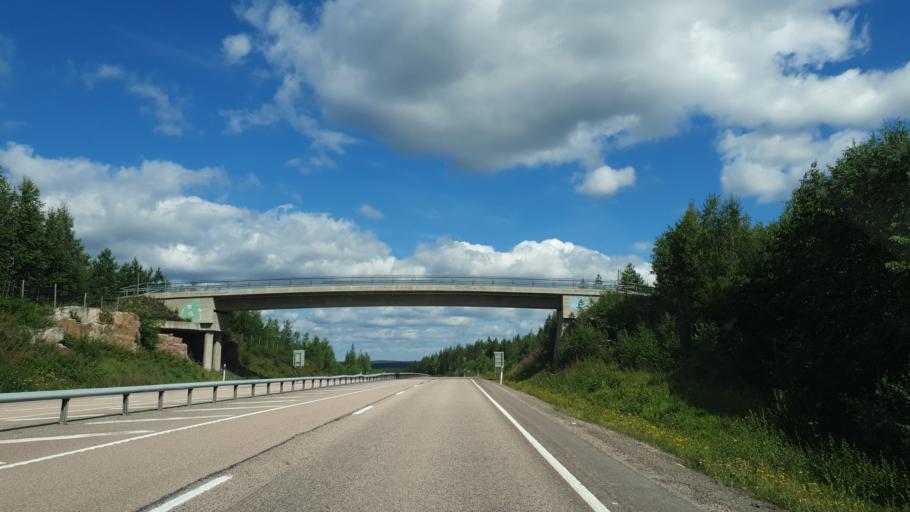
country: FI
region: Central Finland
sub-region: Jaemsae
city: Jaemsae
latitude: 61.7877
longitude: 24.9240
